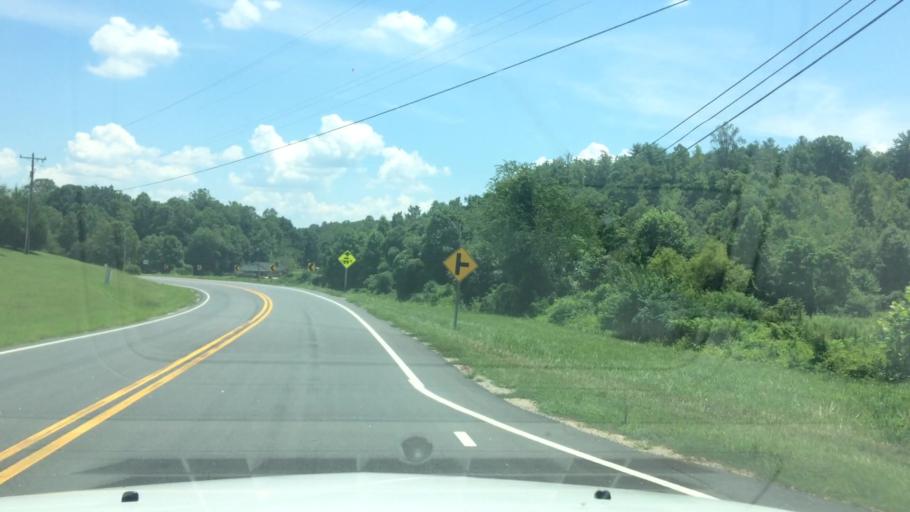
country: US
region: North Carolina
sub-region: Alexander County
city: Taylorsville
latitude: 35.9193
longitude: -81.2550
